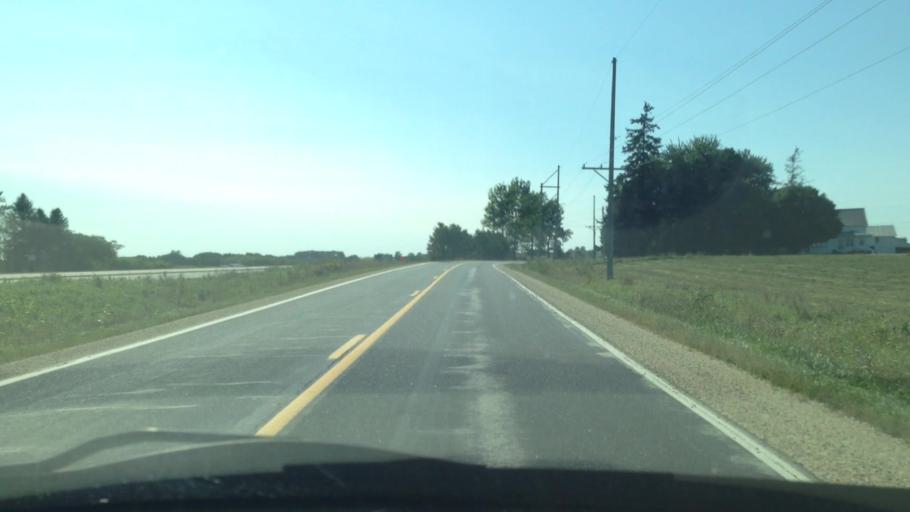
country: US
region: Minnesota
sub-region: Winona County
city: Lewiston
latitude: 43.9408
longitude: -91.7582
